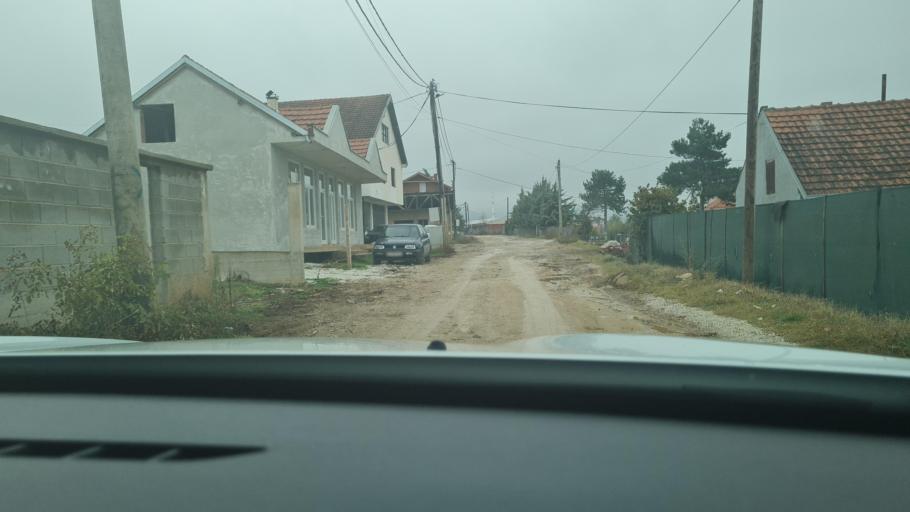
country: MK
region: Opstina Lipkovo
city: Matejche
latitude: 42.1221
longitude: 21.6012
